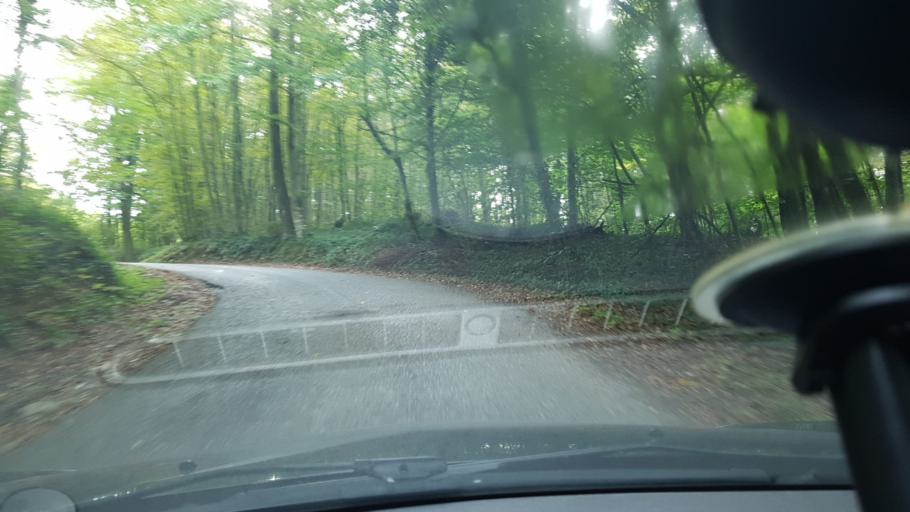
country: HR
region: Krapinsko-Zagorska
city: Radoboj
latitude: 46.1781
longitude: 15.9642
